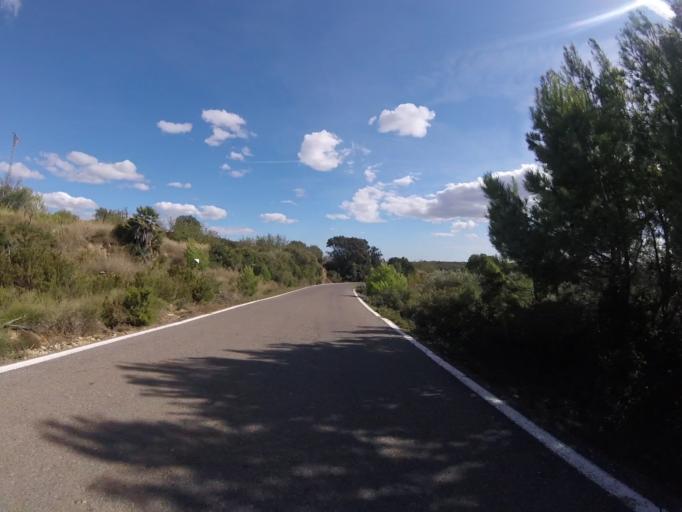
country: ES
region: Valencia
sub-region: Provincia de Castello
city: Albocasser
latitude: 40.3963
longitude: 0.0901
